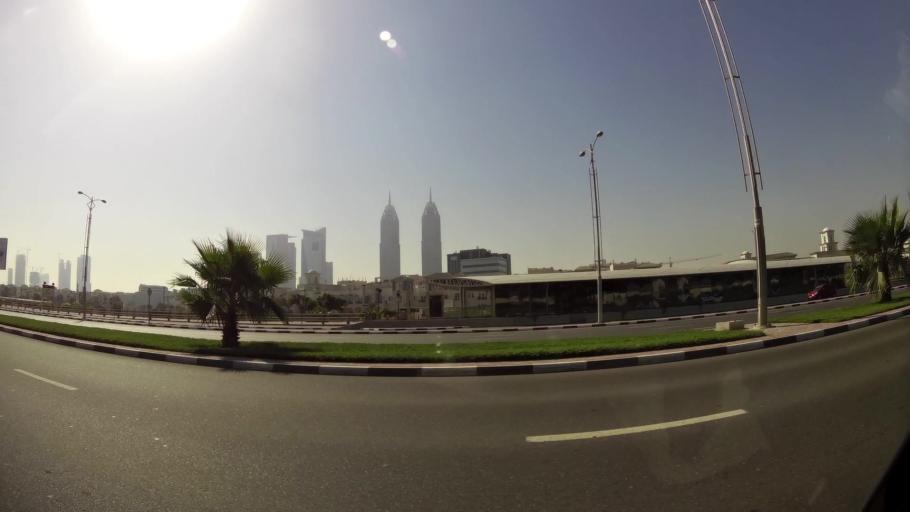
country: AE
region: Dubai
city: Dubai
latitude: 25.1045
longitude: 55.1613
